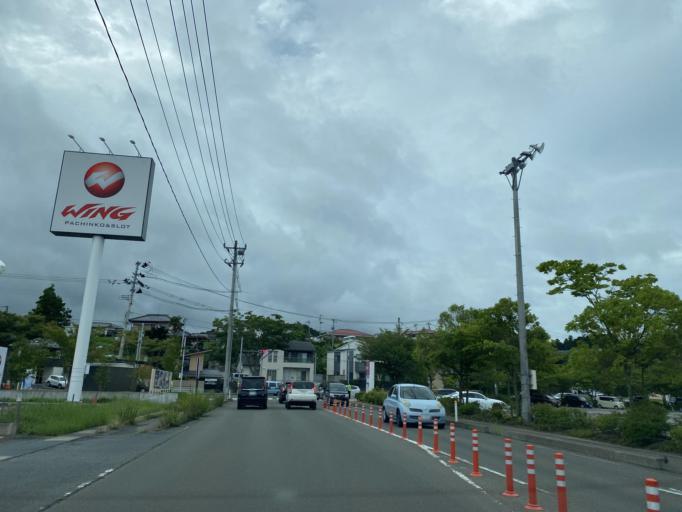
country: JP
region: Miyagi
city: Rifu
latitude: 38.3271
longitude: 140.9703
